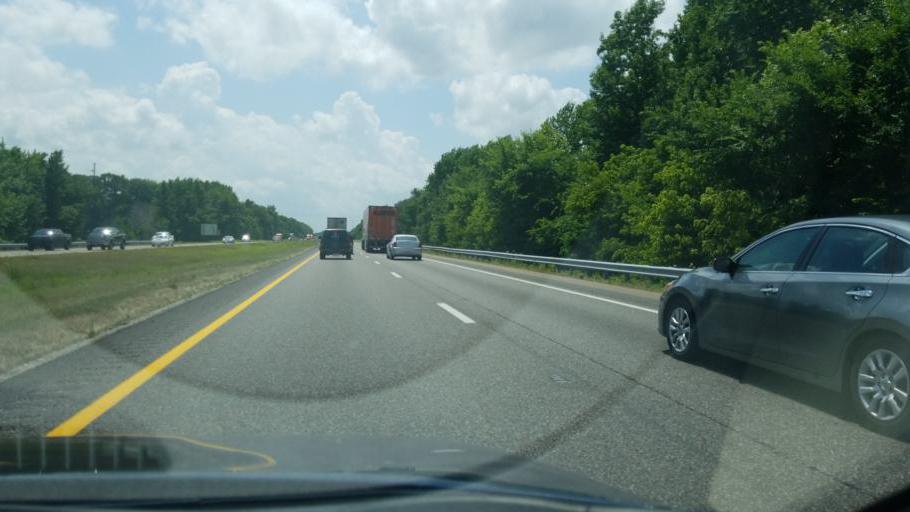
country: US
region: Tennessee
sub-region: Madison County
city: Jackson
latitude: 35.6464
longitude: -88.9035
